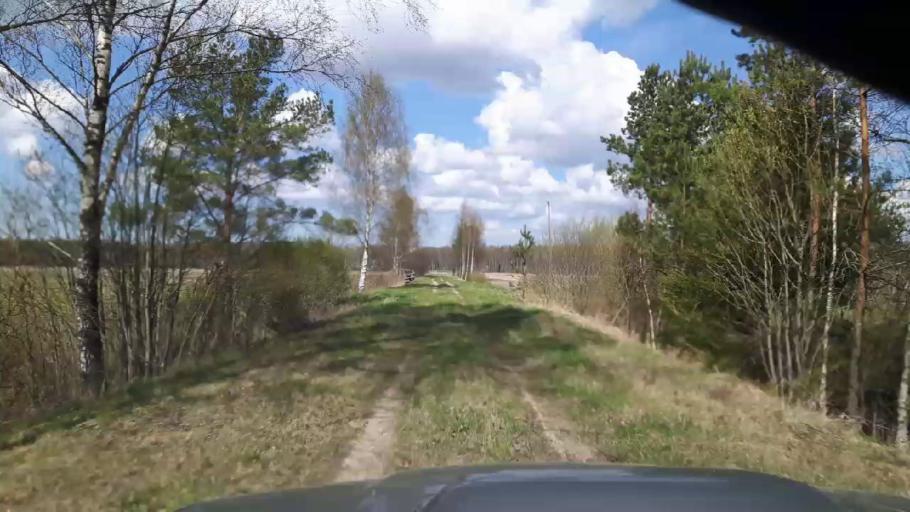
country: EE
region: Paernumaa
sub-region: Vaendra vald (alev)
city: Vandra
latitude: 58.5430
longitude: 25.0799
